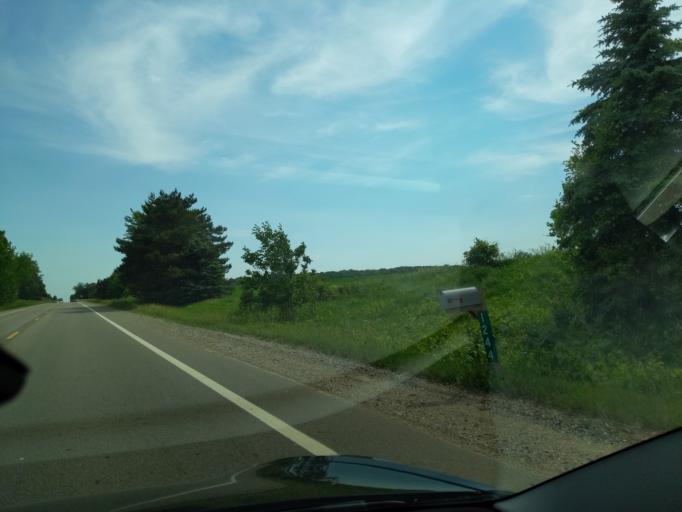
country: US
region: Michigan
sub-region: Barry County
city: Nashville
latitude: 42.6720
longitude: -85.0953
